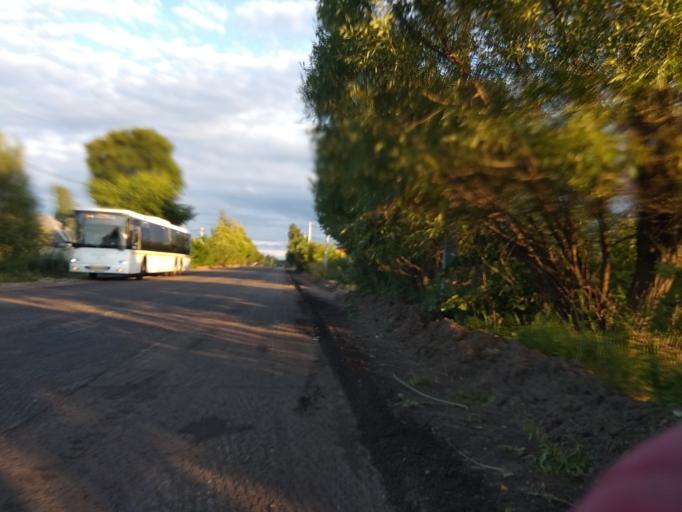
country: RU
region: Moskovskaya
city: Misheronskiy
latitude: 55.6520
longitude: 39.7541
